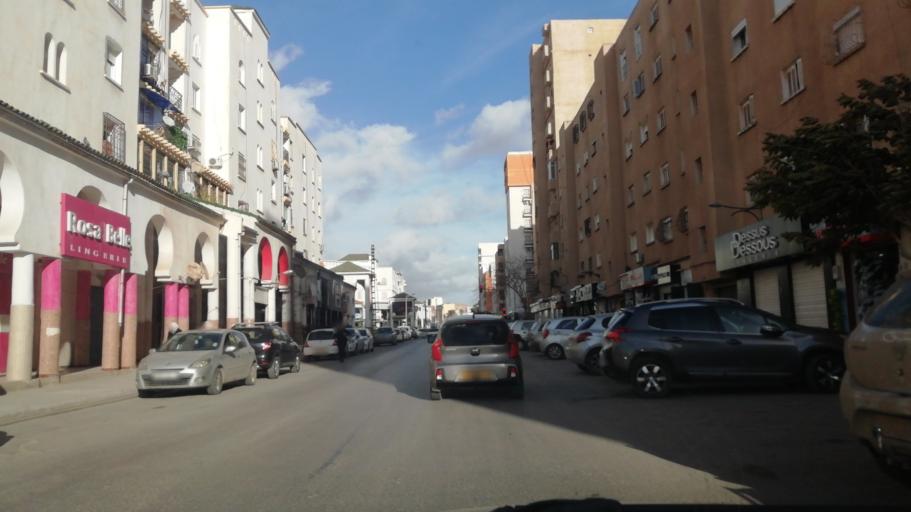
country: DZ
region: Oran
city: Bir el Djir
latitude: 35.7247
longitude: -0.5891
